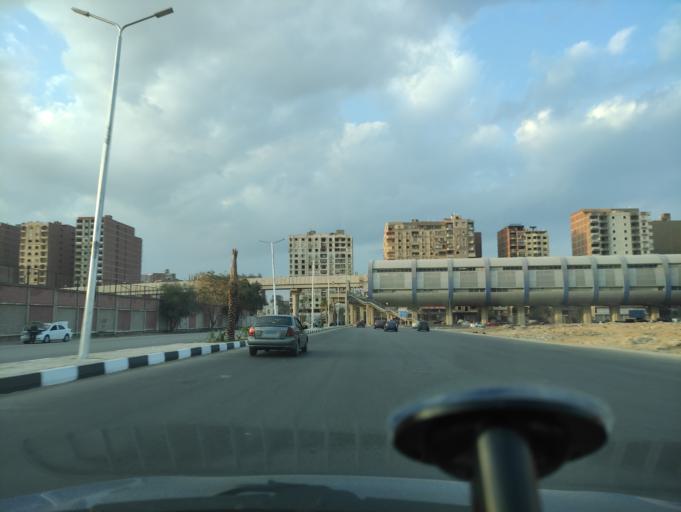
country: EG
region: Muhafazat al Qalyubiyah
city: Al Khankah
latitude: 30.1264
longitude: 31.3603
